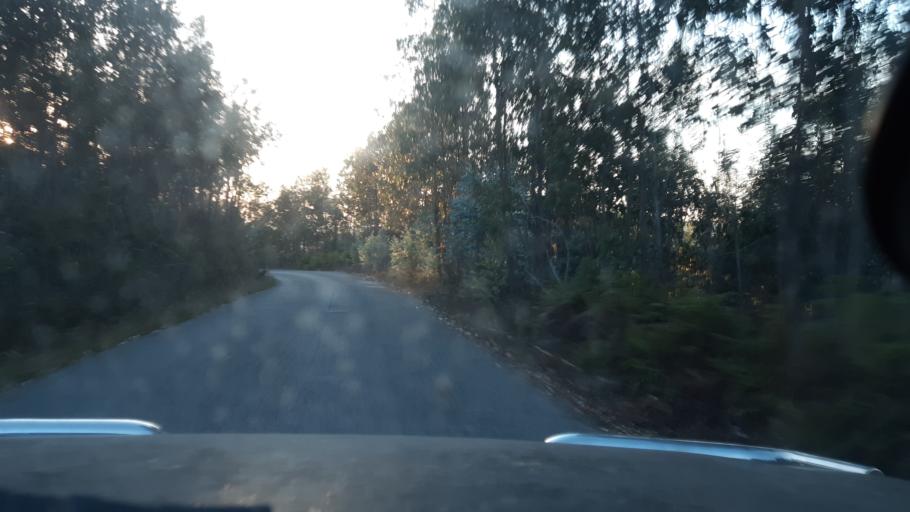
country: PT
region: Aveiro
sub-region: Agueda
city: Aguada de Cima
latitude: 40.5684
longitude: -8.3250
